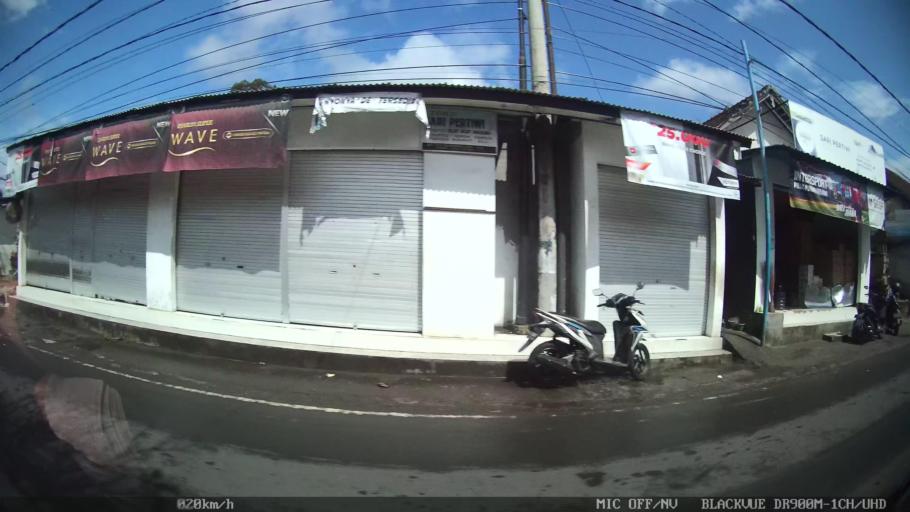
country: ID
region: Bali
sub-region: Kabupaten Gianyar
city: Ubud
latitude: -8.5275
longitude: 115.2637
